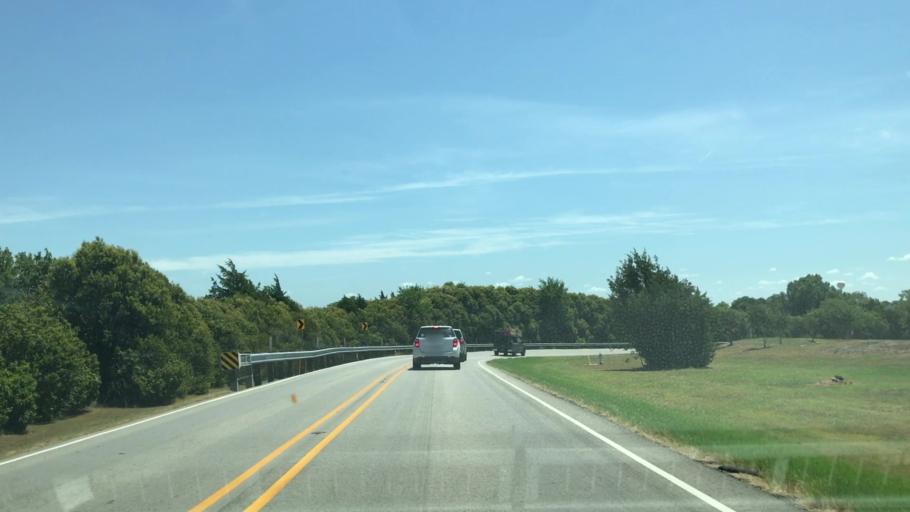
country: US
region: Texas
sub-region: Collin County
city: Lucas
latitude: 33.0748
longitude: -96.5732
